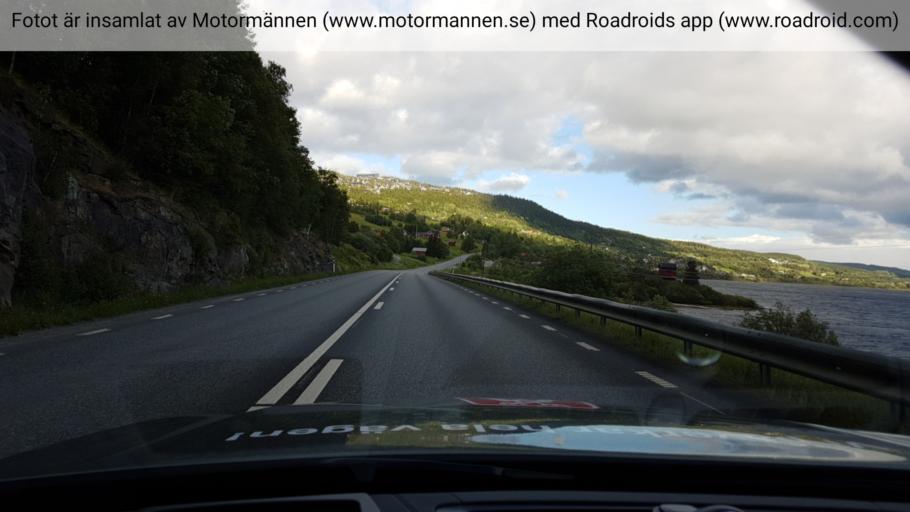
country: SE
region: Jaemtland
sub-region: Are Kommun
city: Are
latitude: 63.3861
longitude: 13.1180
